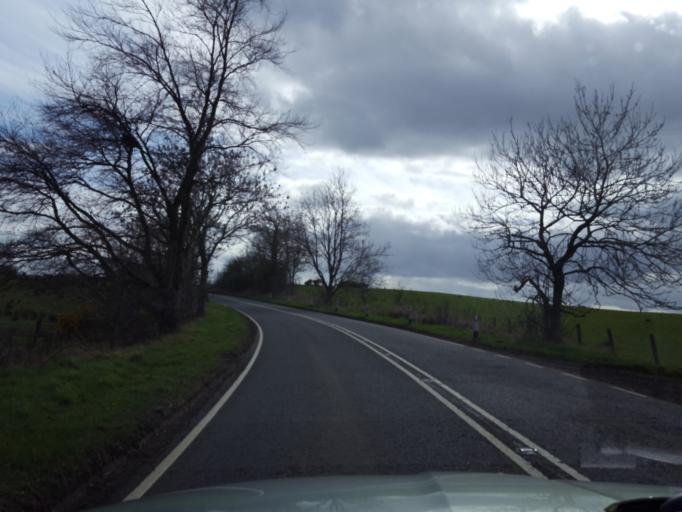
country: GB
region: Scotland
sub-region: West Lothian
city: Bathgate
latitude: 55.9536
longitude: -3.6624
